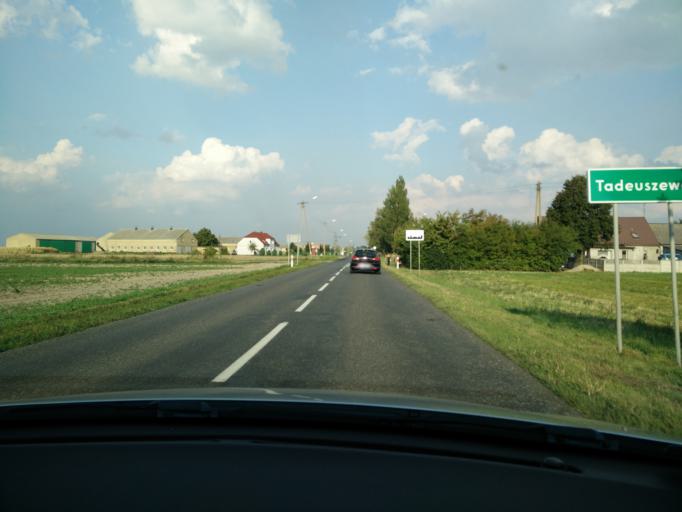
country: PL
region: Greater Poland Voivodeship
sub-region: Powiat sredzki
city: Dominowo
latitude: 52.2407
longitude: 17.3586
